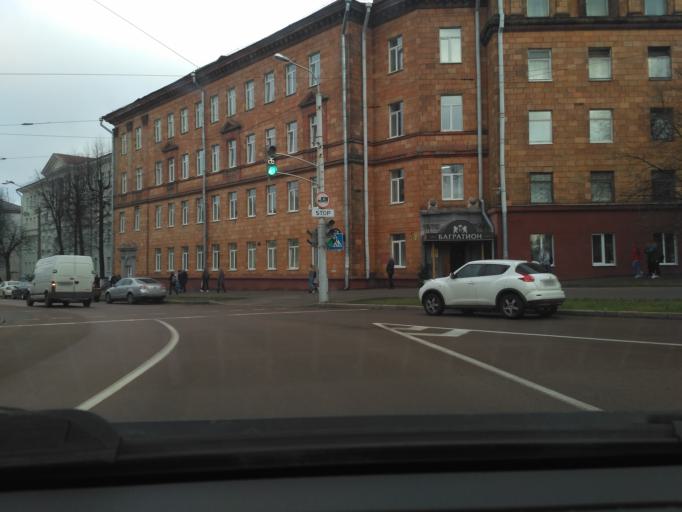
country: BY
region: Minsk
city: Minsk
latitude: 53.9049
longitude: 27.5848
